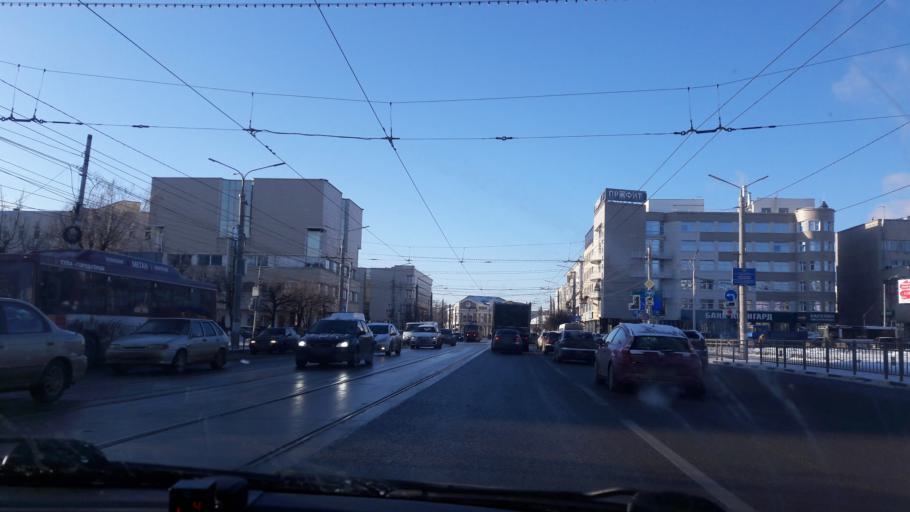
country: RU
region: Tula
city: Tula
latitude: 54.1905
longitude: 37.6265
